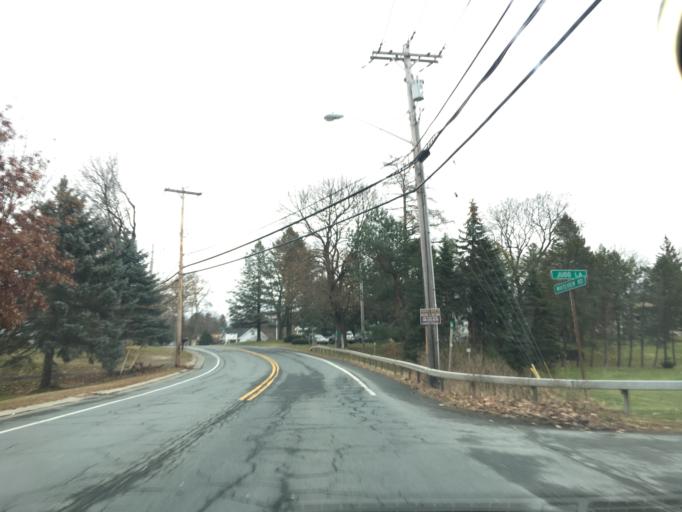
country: US
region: New York
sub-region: Rensselaer County
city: Wynantskill
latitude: 42.6920
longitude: -73.6497
